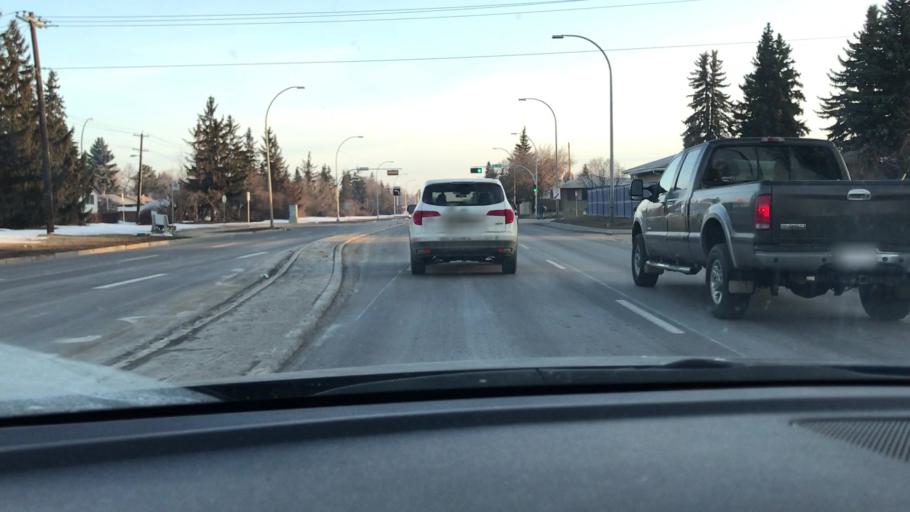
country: CA
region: Alberta
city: Edmonton
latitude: 53.5204
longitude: -113.4429
